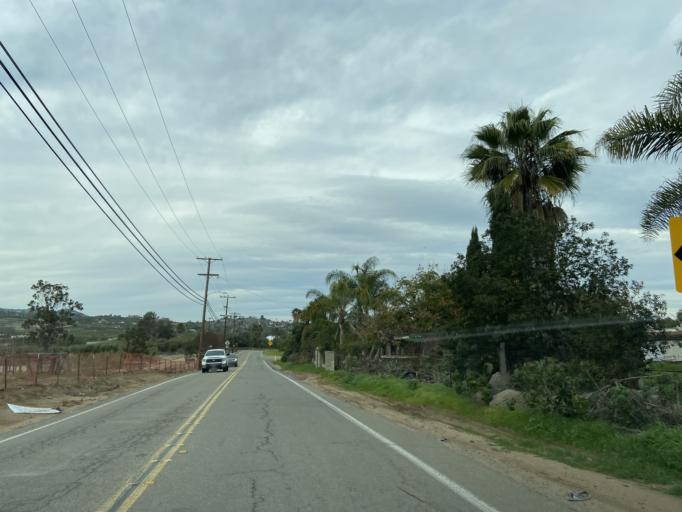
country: US
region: California
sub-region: San Diego County
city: Bonsall
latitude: 33.2637
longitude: -117.2450
